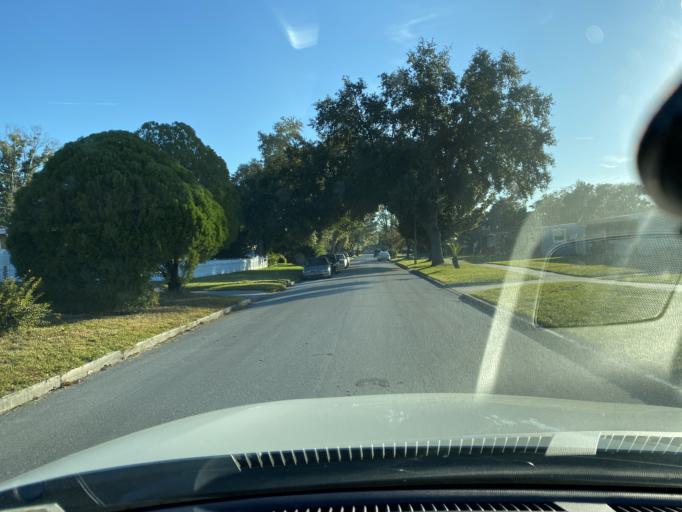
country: US
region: Florida
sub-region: Orange County
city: Azalea Park
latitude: 28.5353
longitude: -81.3056
